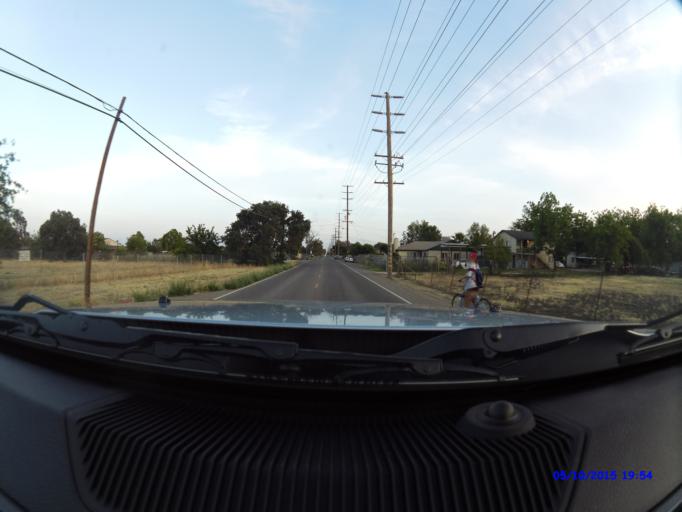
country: US
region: California
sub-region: San Joaquin County
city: Kennedy
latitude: 37.9331
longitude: -121.2465
